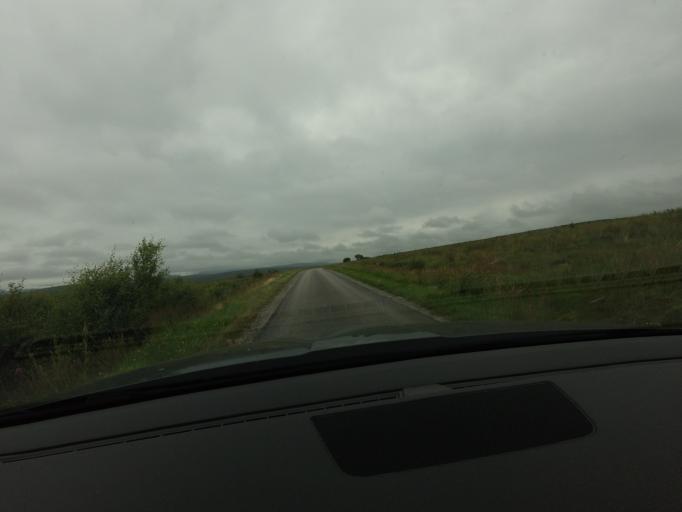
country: GB
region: Scotland
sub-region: Highland
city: Evanton
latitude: 58.1748
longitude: -4.5122
